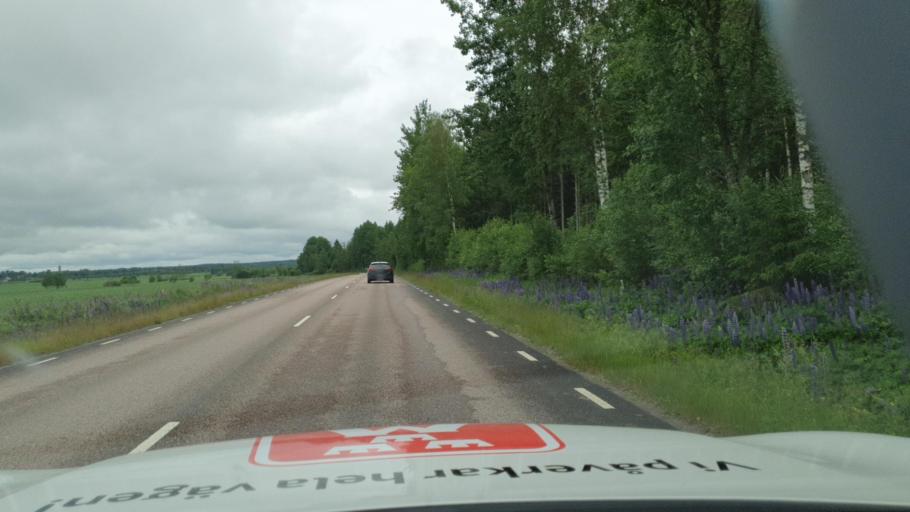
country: SE
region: Vaermland
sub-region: Karlstads Kommun
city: Edsvalla
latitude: 59.4126
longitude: 13.2143
